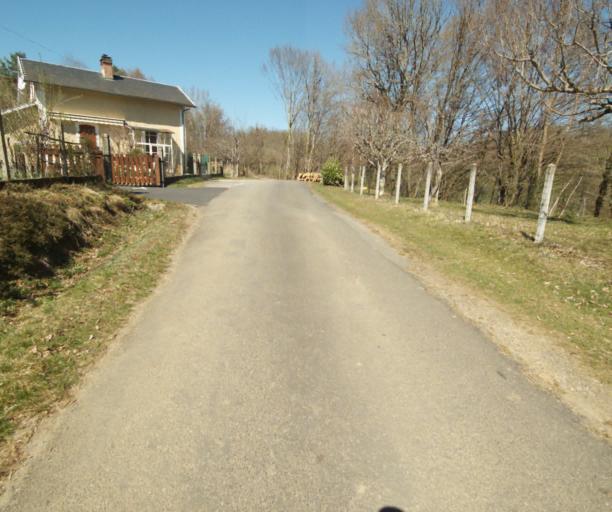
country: FR
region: Limousin
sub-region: Departement de la Correze
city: Saint-Clement
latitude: 45.3177
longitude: 1.7040
